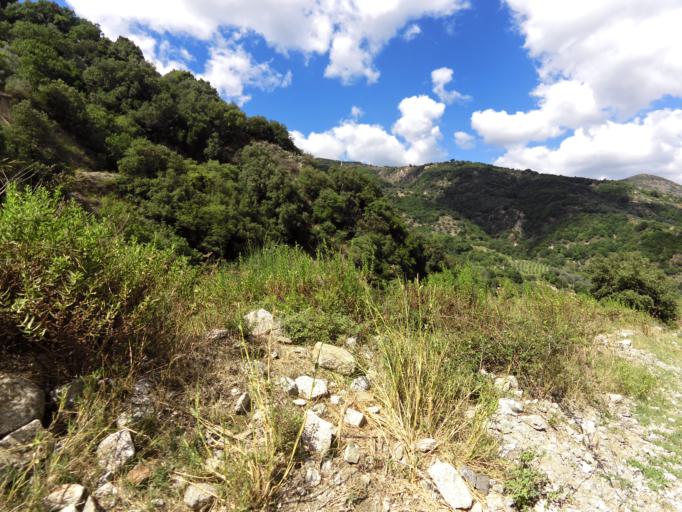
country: IT
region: Calabria
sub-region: Provincia di Reggio Calabria
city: Bivongi
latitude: 38.4857
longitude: 16.4259
